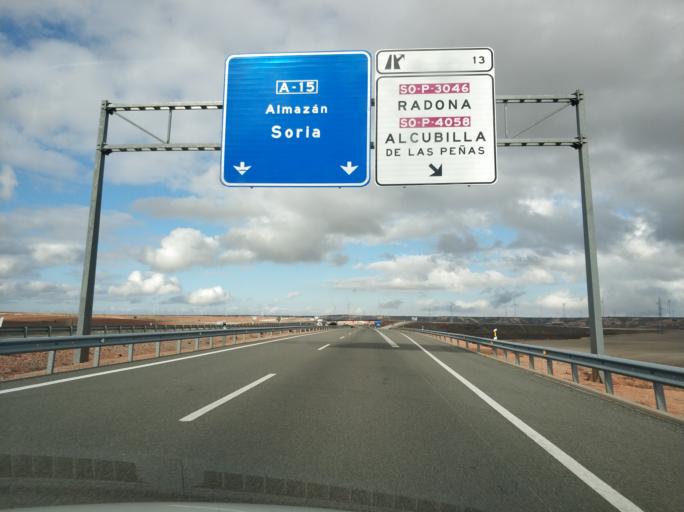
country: ES
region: Castille and Leon
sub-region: Provincia de Soria
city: Alcubilla de las Penas
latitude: 41.2553
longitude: -2.4735
